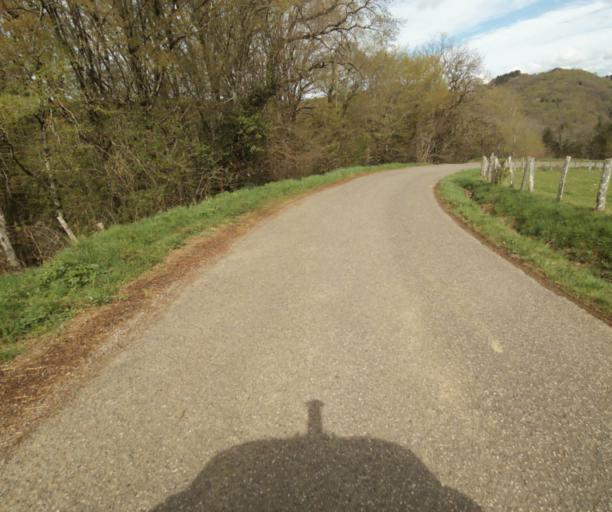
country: FR
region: Limousin
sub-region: Departement de la Correze
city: Laguenne
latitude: 45.2509
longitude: 1.8285
